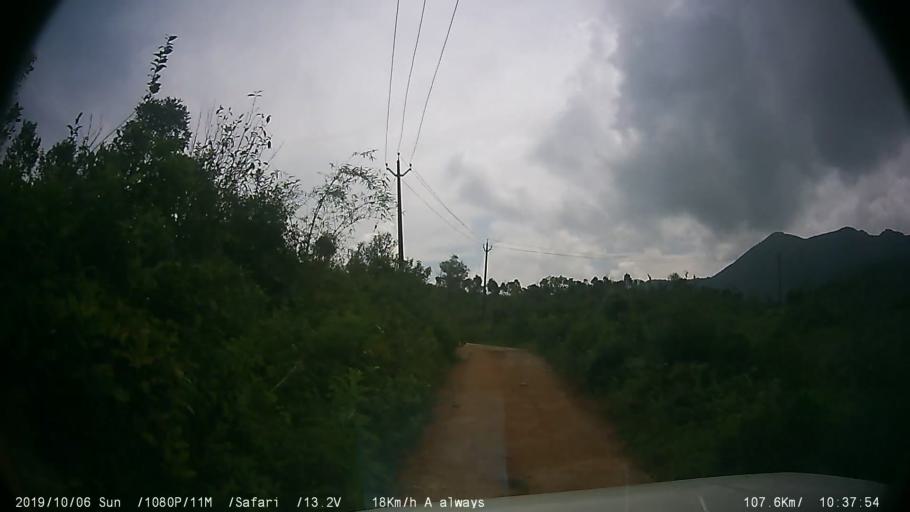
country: IN
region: Kerala
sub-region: Kottayam
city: Erattupetta
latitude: 9.6193
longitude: 76.9354
